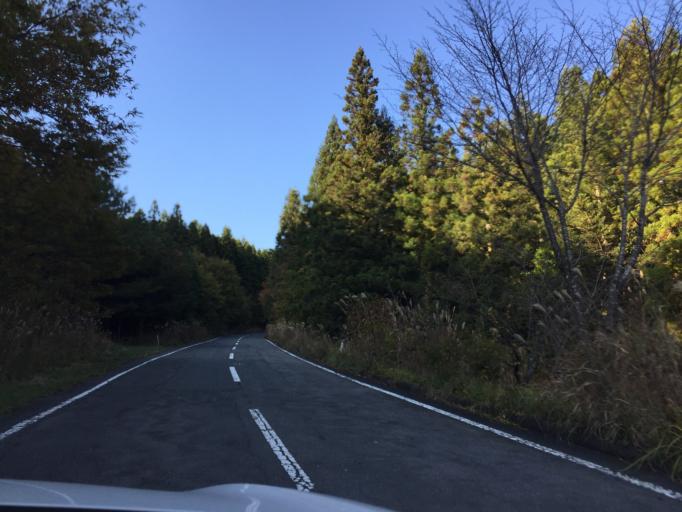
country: JP
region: Fukushima
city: Funehikimachi-funehiki
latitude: 37.2751
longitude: 140.7645
